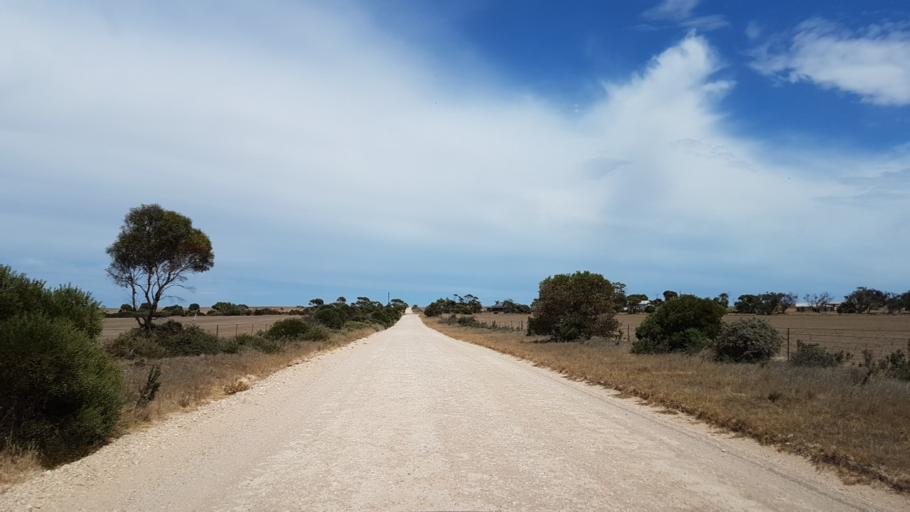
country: AU
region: South Australia
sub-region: Yorke Peninsula
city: Ardrossan
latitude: -34.3990
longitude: 137.9207
